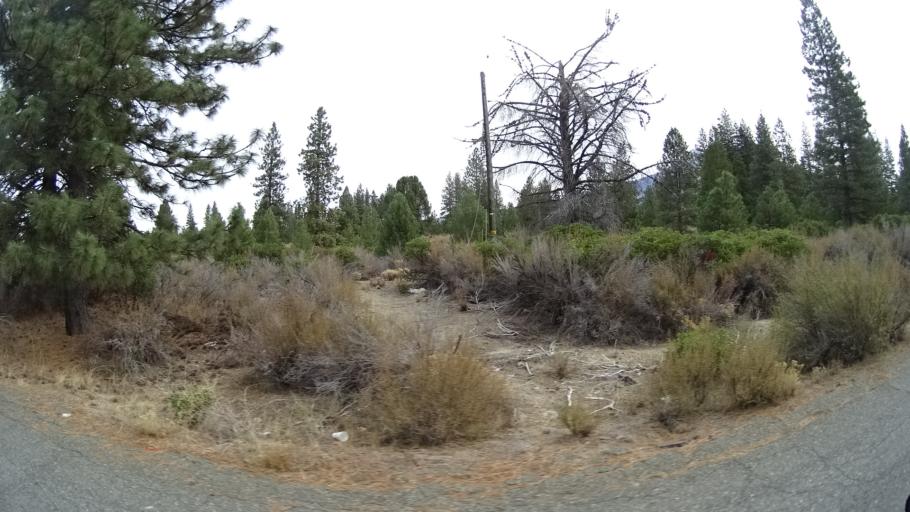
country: US
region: California
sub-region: Siskiyou County
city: Weed
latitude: 41.3958
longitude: -122.3747
